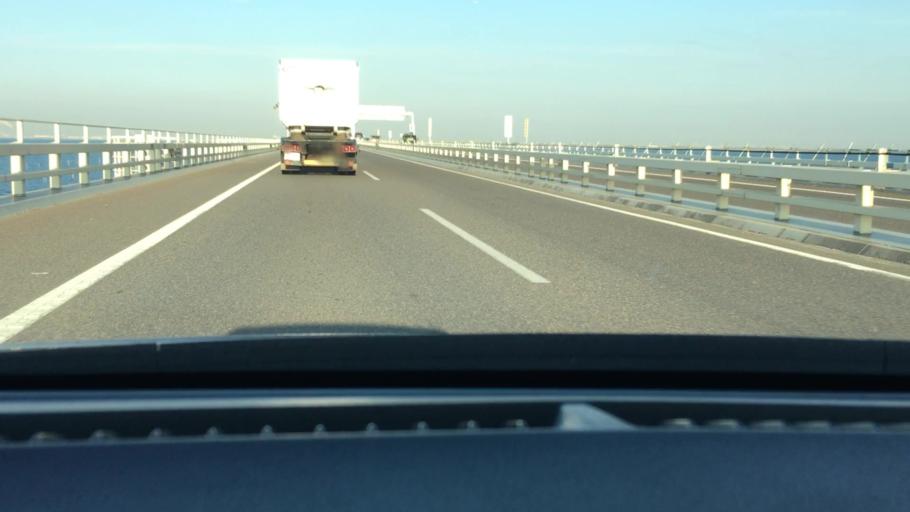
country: JP
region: Chiba
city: Kisarazu
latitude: 35.4393
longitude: 139.9109
